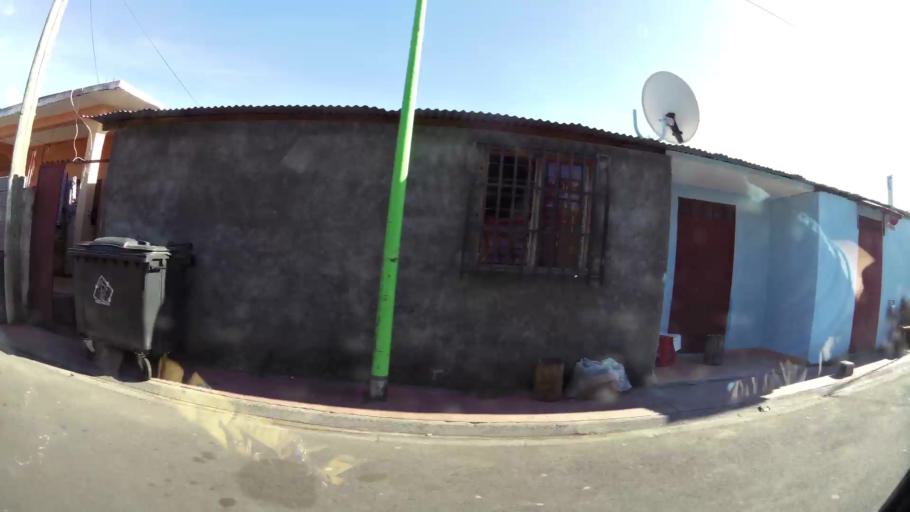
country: YT
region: Pamandzi
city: Pamandzi
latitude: -12.7997
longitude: 45.2758
